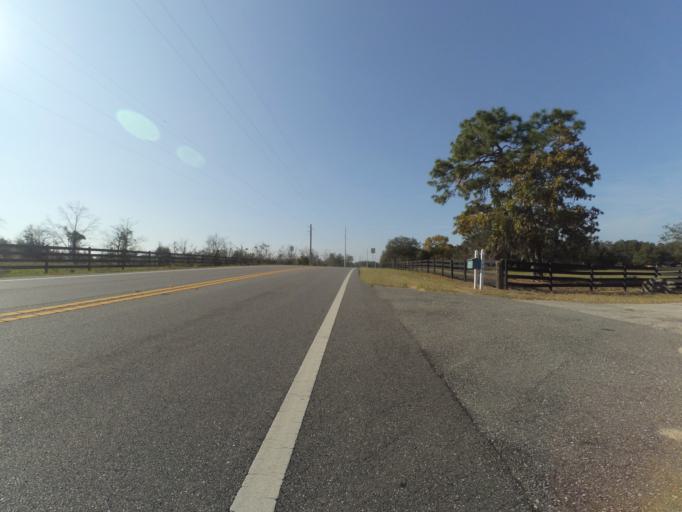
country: US
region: Florida
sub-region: Lake County
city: Umatilla
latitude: 28.9688
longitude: -81.6680
